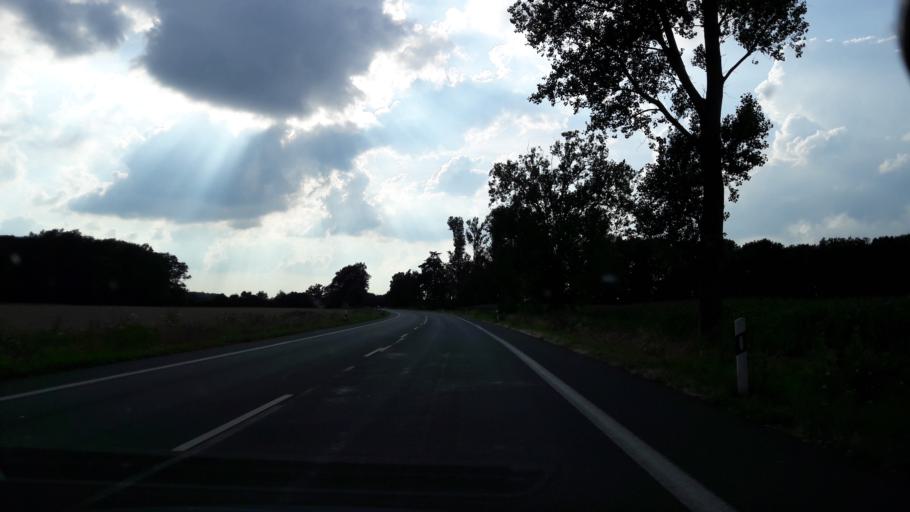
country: DE
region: North Rhine-Westphalia
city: Ahlen
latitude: 51.8256
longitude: 7.8930
